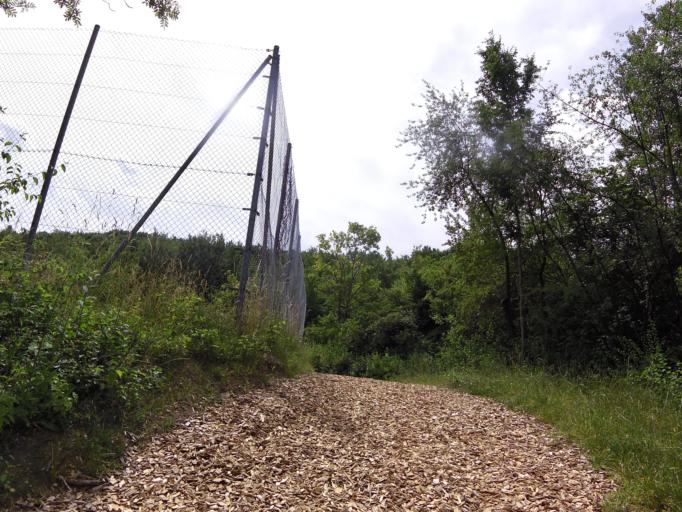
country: DE
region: Bavaria
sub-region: Regierungsbezirk Unterfranken
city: Wuerzburg
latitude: 49.7951
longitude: 9.9661
